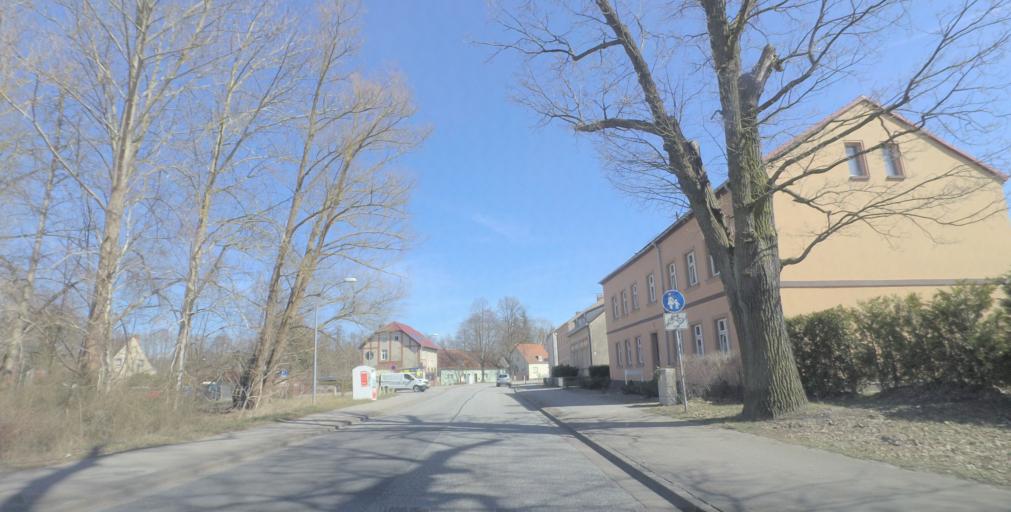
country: DE
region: Brandenburg
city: Neuruppin
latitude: 52.9517
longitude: 12.8385
